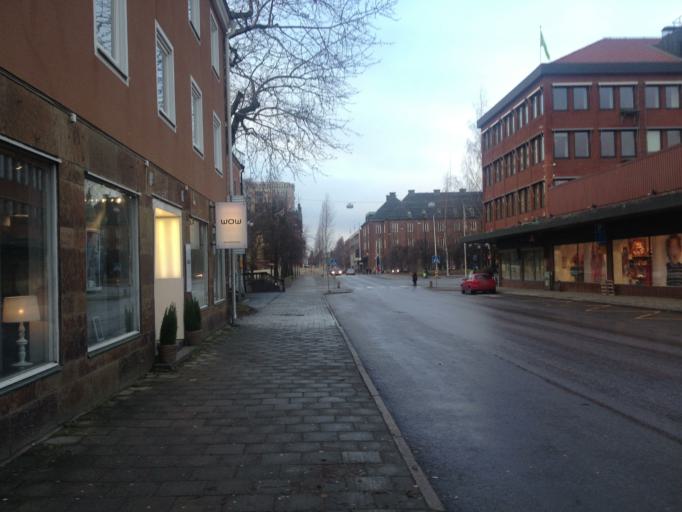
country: SE
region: Vaesterbotten
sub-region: Umea Kommun
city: Umea
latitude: 63.8246
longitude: 20.2647
